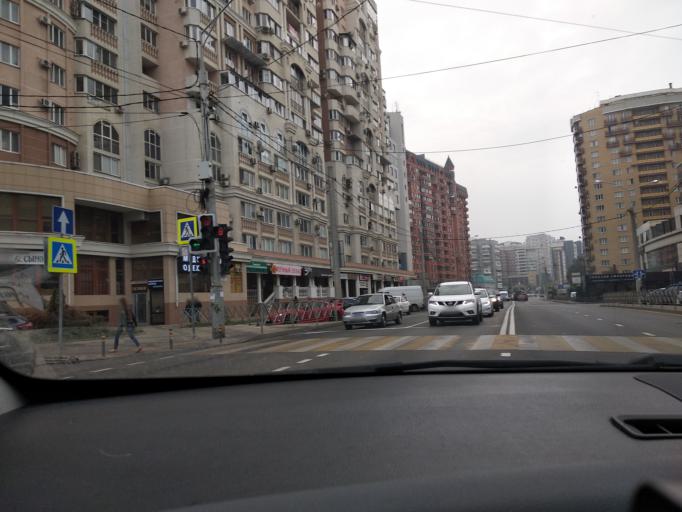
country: RU
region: Krasnodarskiy
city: Krasnodar
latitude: 45.0221
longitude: 38.9598
